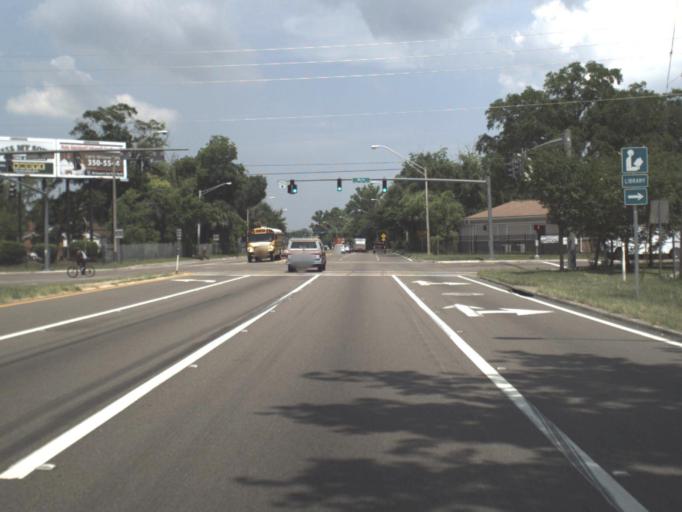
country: US
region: Florida
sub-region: Duval County
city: Jacksonville
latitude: 30.3555
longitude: -81.6766
